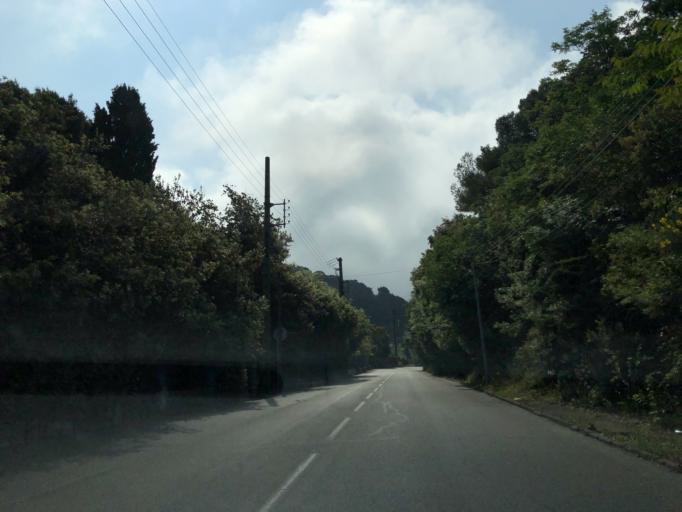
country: FR
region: Provence-Alpes-Cote d'Azur
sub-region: Departement des Alpes-Maritimes
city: Villefranche-sur-Mer
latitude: 43.7193
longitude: 7.3088
